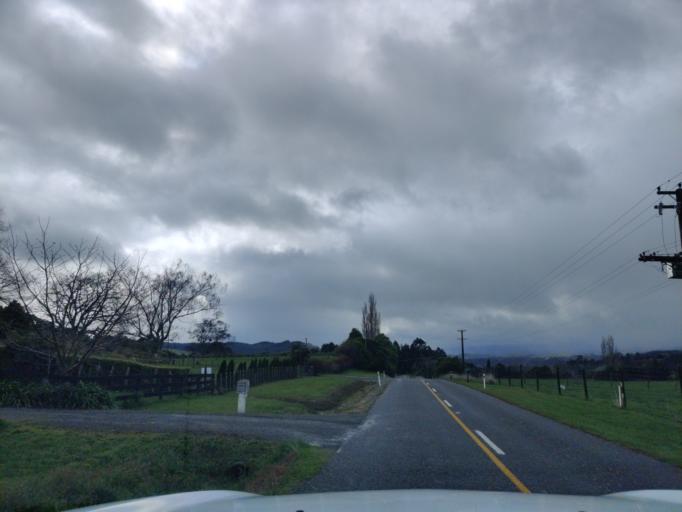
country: NZ
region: Manawatu-Wanganui
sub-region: Palmerston North City
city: Palmerston North
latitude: -40.1848
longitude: 175.7856
